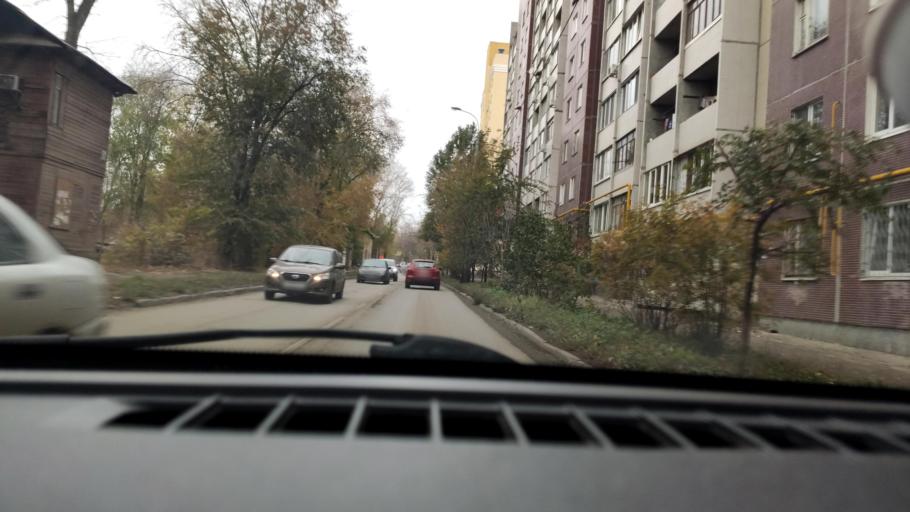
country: RU
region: Samara
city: Samara
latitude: 53.2365
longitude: 50.2626
